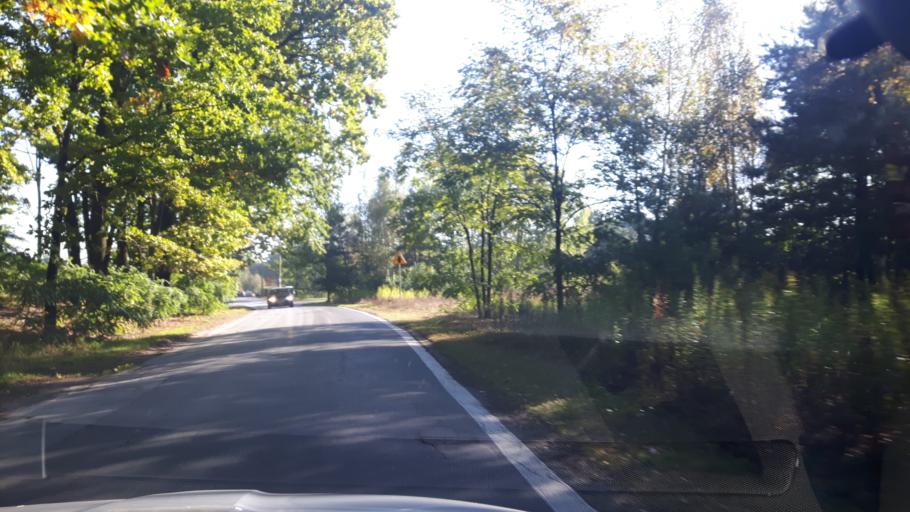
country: PL
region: Masovian Voivodeship
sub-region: Powiat legionowski
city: Stanislawow Pierwszy
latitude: 52.3496
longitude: 21.0113
